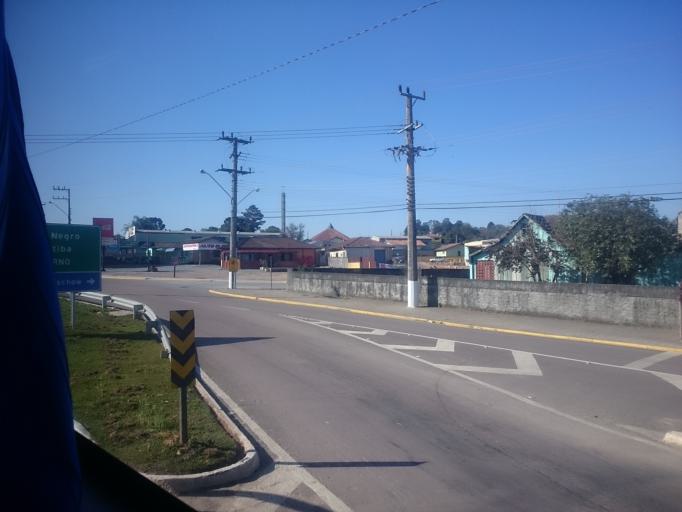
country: BR
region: Parana
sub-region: Rio Negro
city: Rio Negro
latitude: -26.0884
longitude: -49.7799
